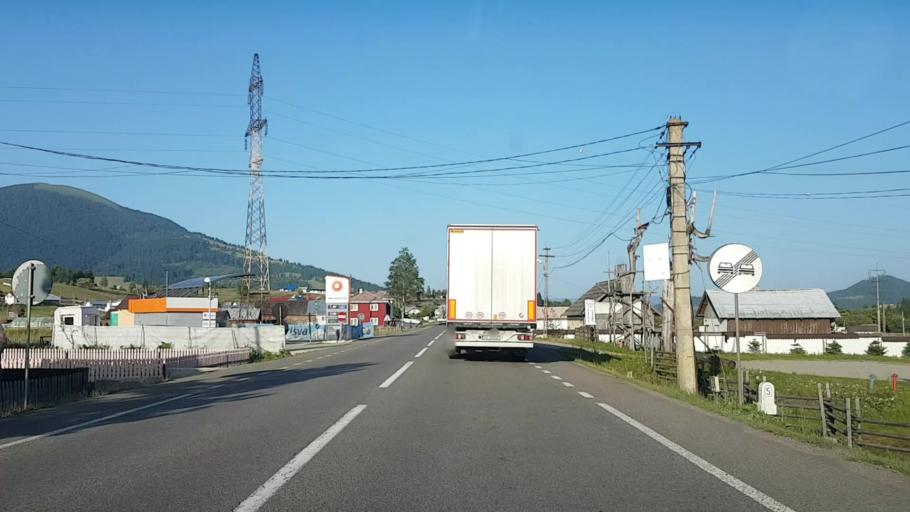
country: RO
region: Suceava
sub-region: Comuna Cosna
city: Cosna
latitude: 47.3608
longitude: 25.1973
